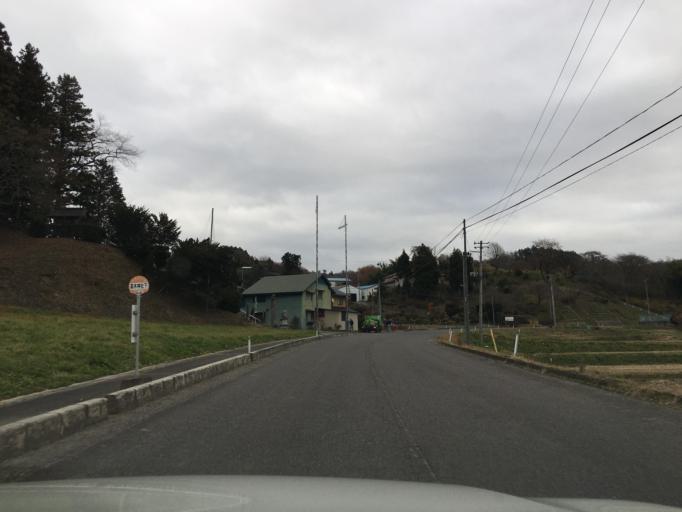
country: JP
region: Fukushima
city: Funehikimachi-funehiki
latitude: 37.4777
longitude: 140.5451
